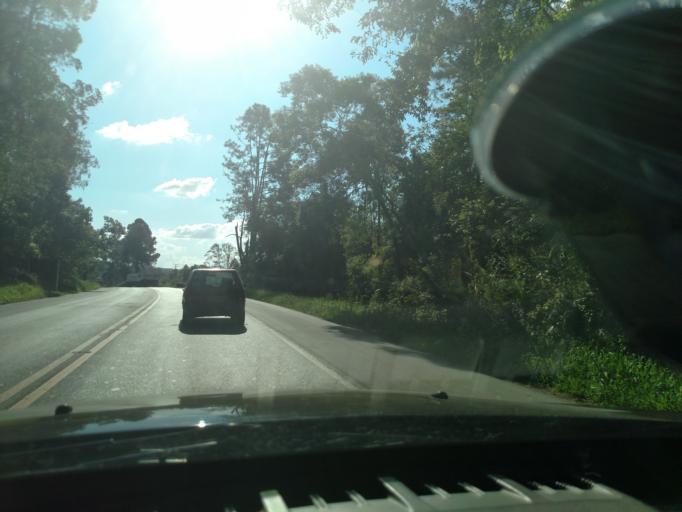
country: BR
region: Santa Catarina
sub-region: Rio Do Sul
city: Rio do Sul
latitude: -27.2857
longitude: -49.7860
